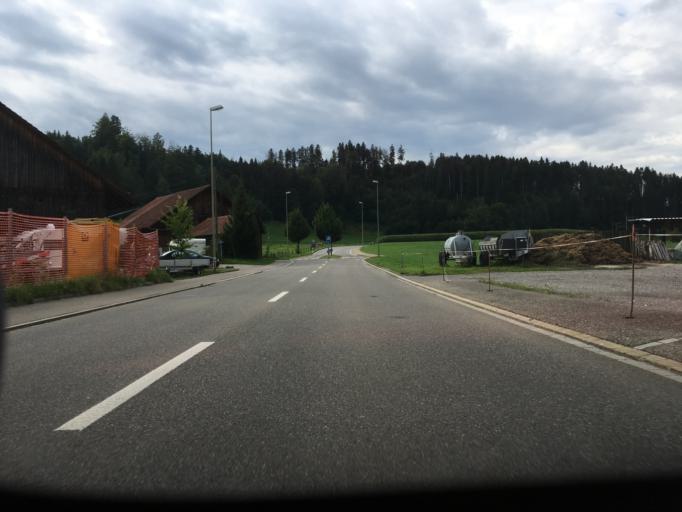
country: CH
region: Zurich
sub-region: Bezirk Pfaeffikon
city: Bauma
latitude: 47.3815
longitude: 8.8586
